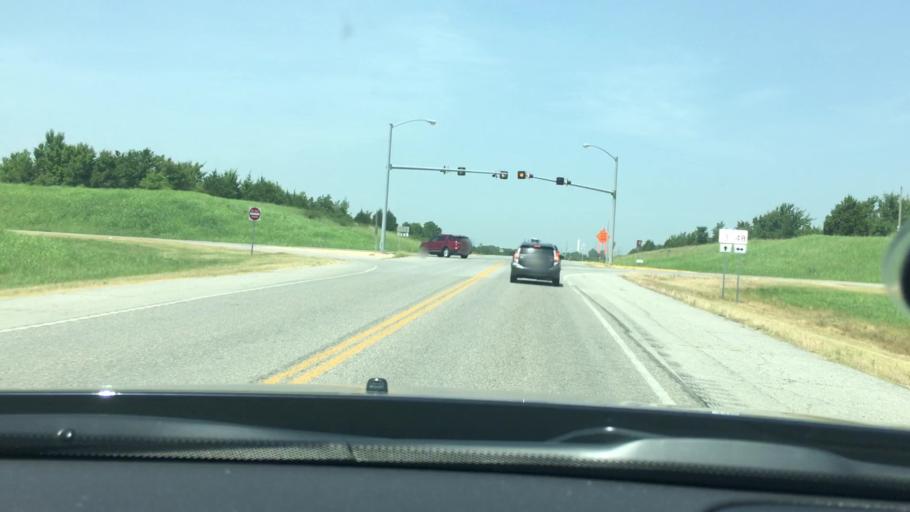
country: US
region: Oklahoma
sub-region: Coal County
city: Coalgate
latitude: 34.6110
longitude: -96.4236
